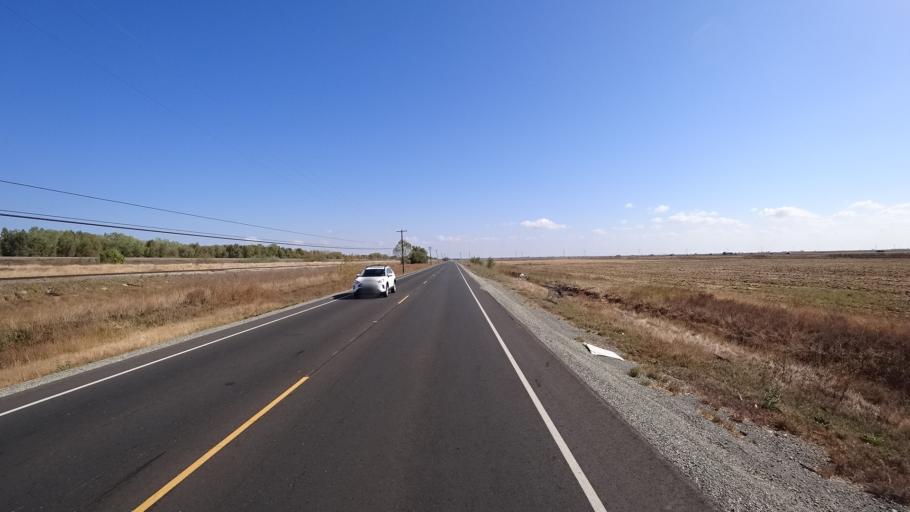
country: US
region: California
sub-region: Yolo County
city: Woodland
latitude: 38.6768
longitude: -121.6997
